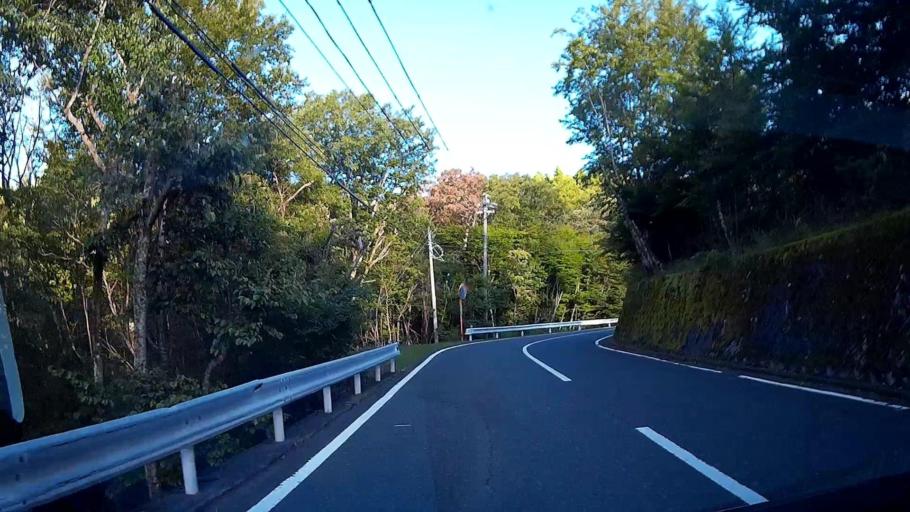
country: JP
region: Shizuoka
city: Shizuoka-shi
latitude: 35.2045
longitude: 138.2531
